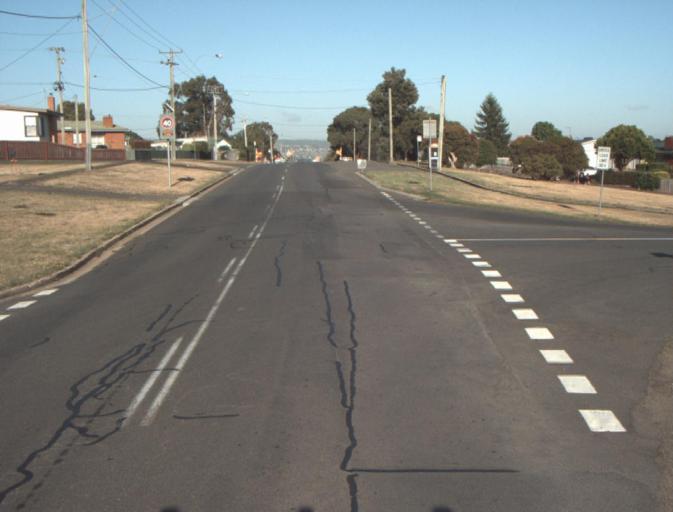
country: AU
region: Tasmania
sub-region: Launceston
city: Newstead
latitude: -41.4345
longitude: 147.1905
